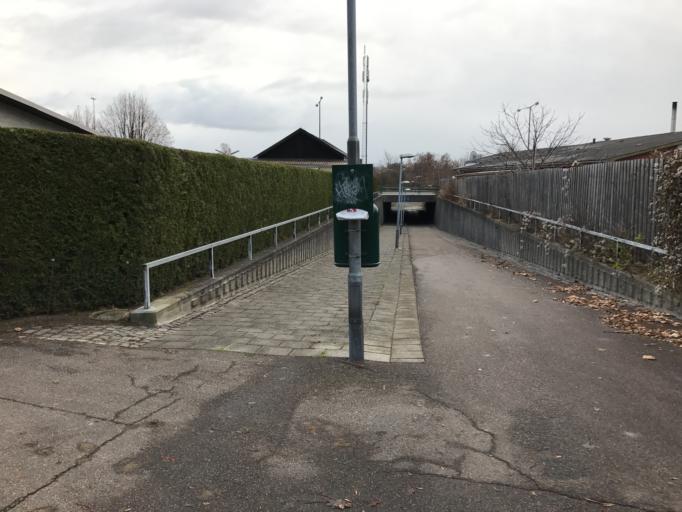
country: DK
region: Capital Region
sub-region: Hoje-Taastrup Kommune
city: Taastrup
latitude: 55.6585
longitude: 12.2972
